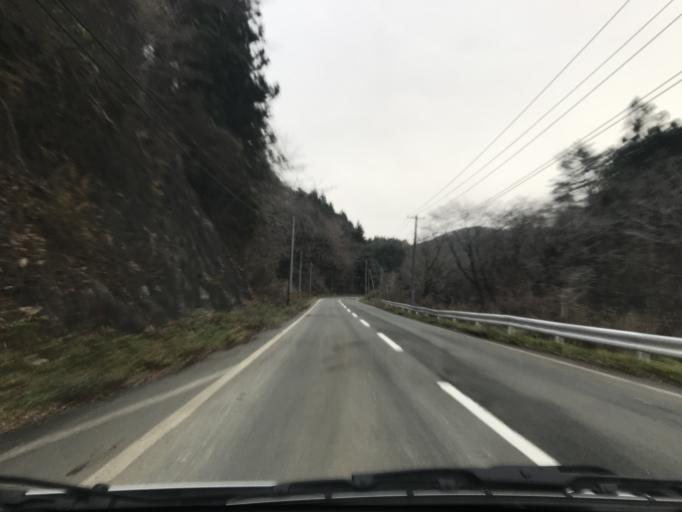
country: JP
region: Iwate
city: Tono
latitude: 39.1821
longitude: 141.3599
